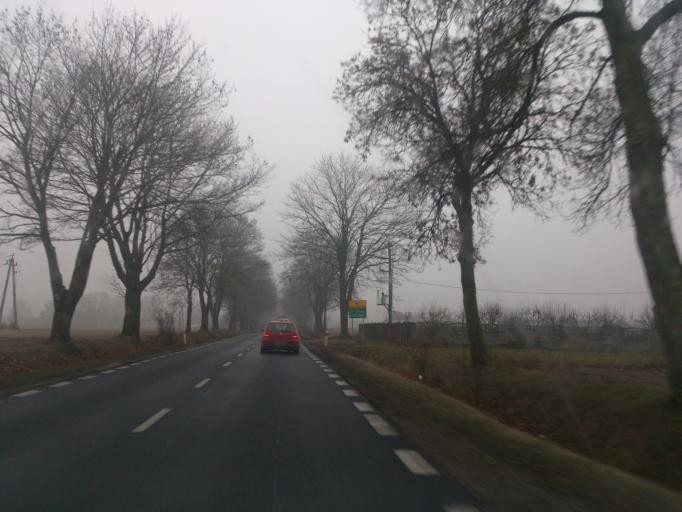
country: PL
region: Masovian Voivodeship
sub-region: Powiat sierpecki
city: Sierpc
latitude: 52.8719
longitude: 19.6610
